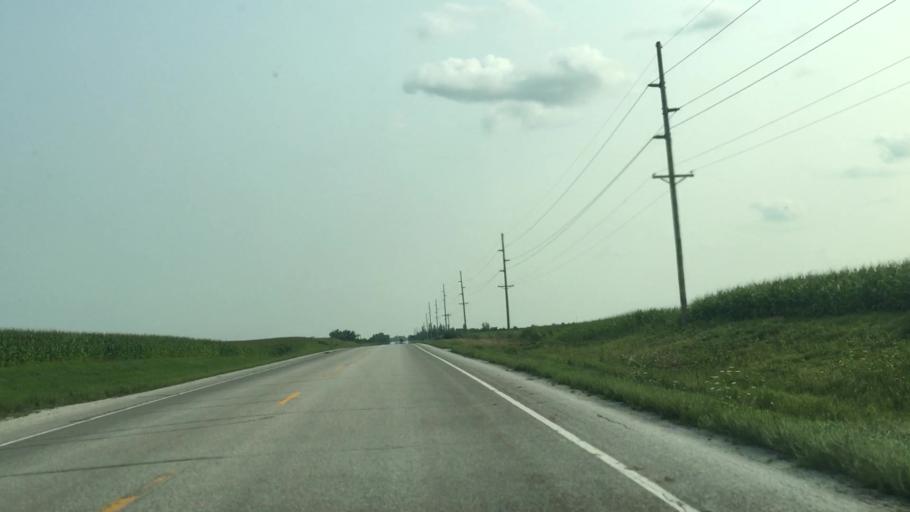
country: US
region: Minnesota
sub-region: Fillmore County
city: Harmony
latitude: 43.5607
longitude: -91.9298
